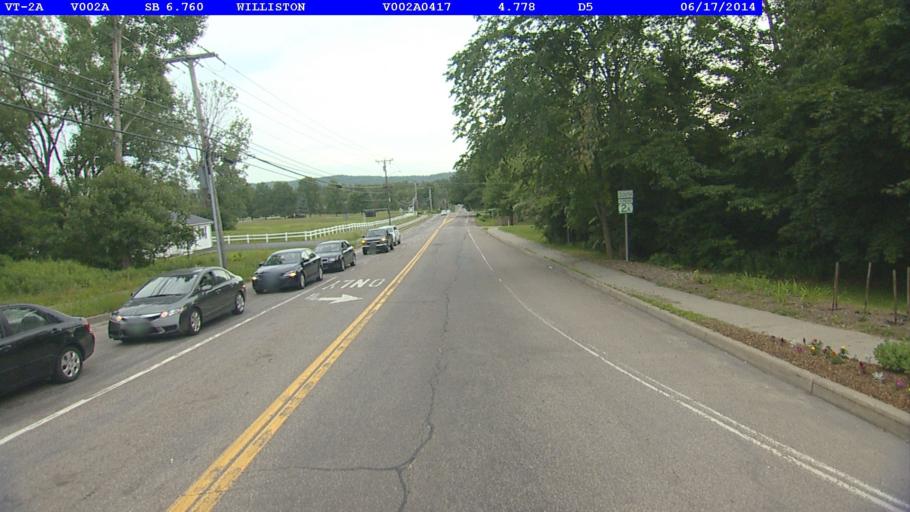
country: US
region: Vermont
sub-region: Chittenden County
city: Essex Junction
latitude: 44.4648
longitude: -73.1129
